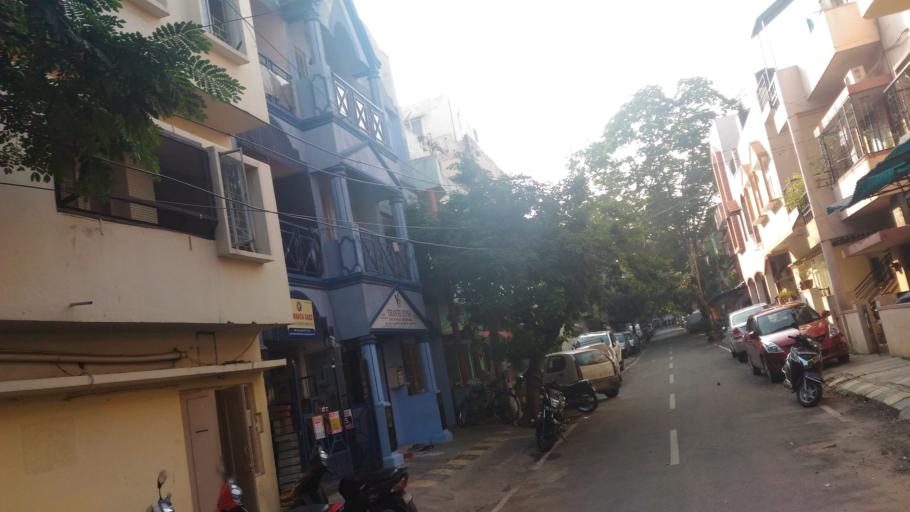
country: IN
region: Karnataka
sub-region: Bangalore Urban
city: Bangalore
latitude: 12.9222
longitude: 77.5970
